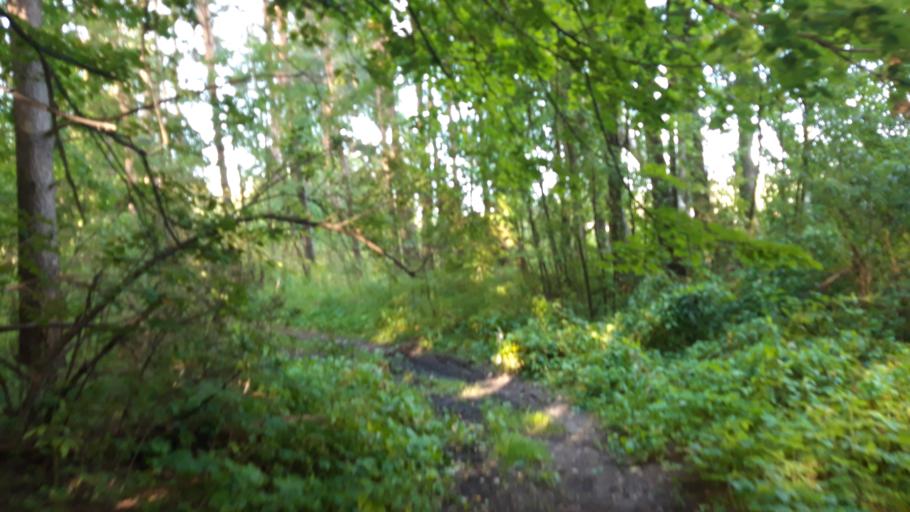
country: RU
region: Tverskaya
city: Konakovo
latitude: 56.6959
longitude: 36.7285
